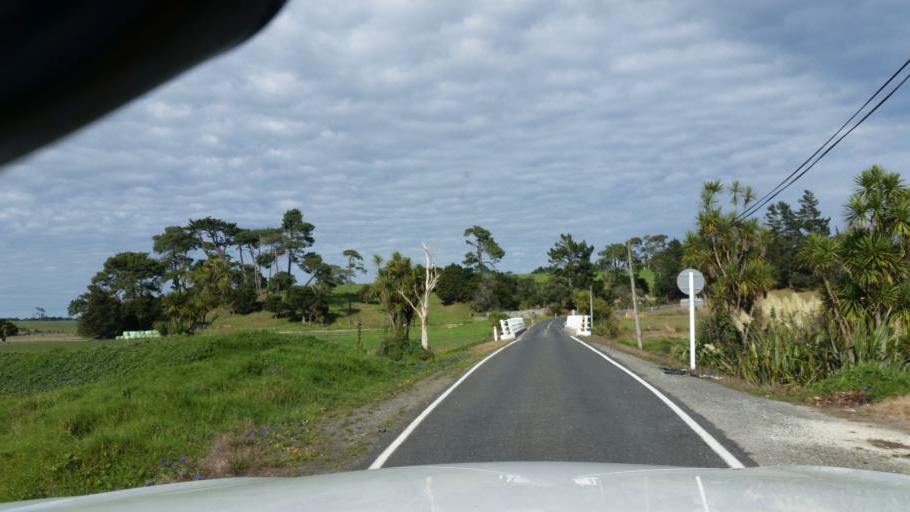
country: NZ
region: Northland
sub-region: Kaipara District
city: Dargaville
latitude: -35.9136
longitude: 173.8330
